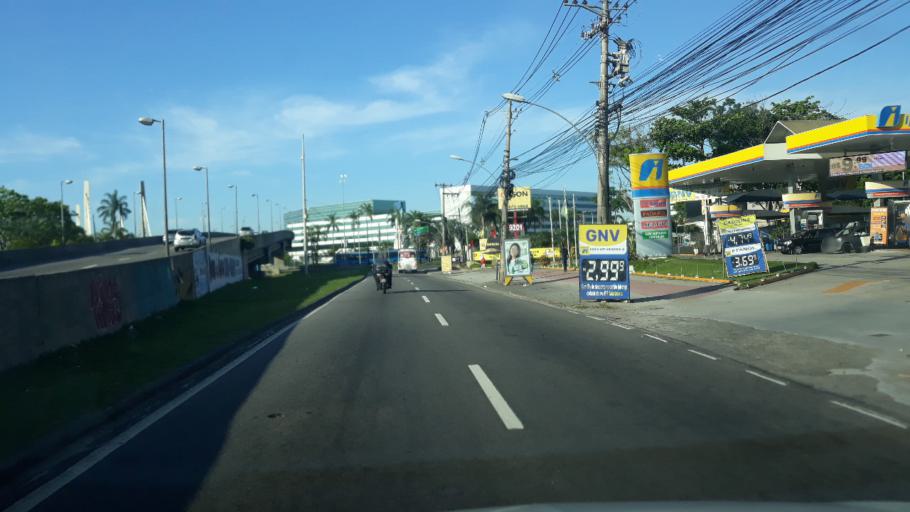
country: BR
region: Rio de Janeiro
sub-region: Sao Joao De Meriti
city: Sao Joao de Meriti
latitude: -22.9723
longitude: -43.3627
